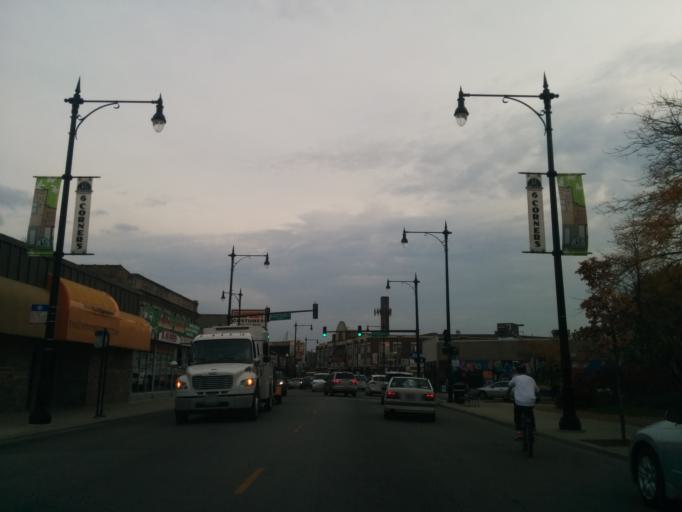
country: US
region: Illinois
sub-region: Cook County
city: Lincolnwood
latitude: 41.9556
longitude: -87.7502
